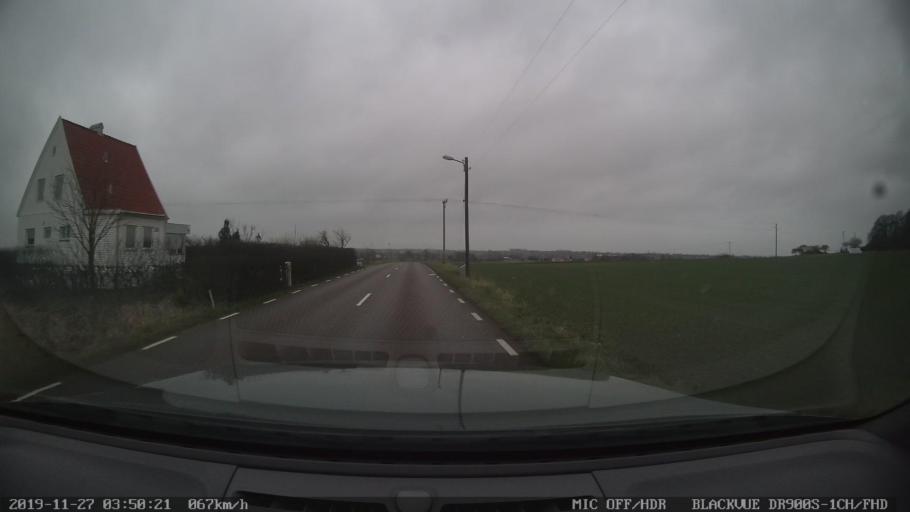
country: SE
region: Skane
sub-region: Hoganas Kommun
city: Hoganas
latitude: 56.2534
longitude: 12.5698
